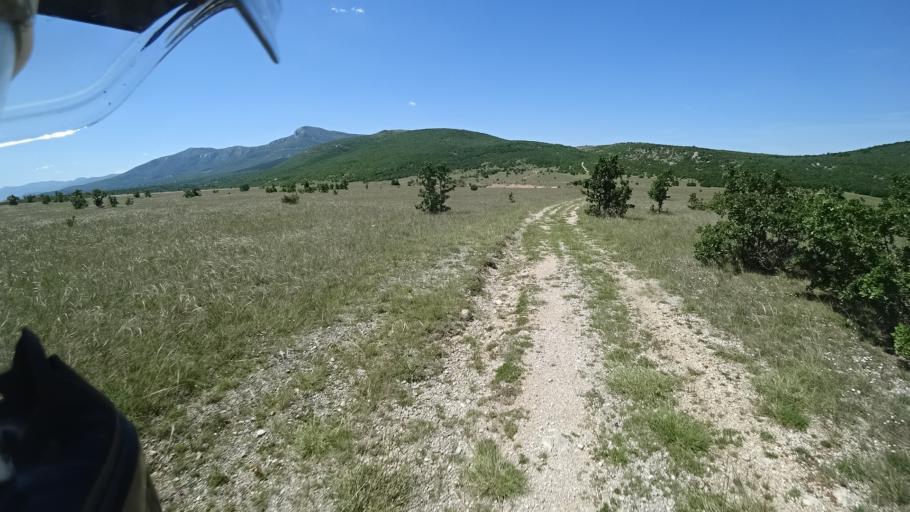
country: HR
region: Sibensko-Kniniska
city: Knin
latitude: 44.0172
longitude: 16.3477
